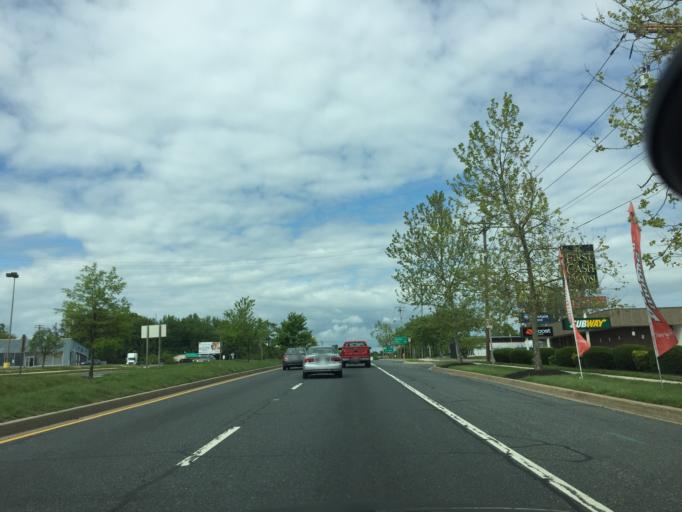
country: US
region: Maryland
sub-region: Baltimore County
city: Essex
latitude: 39.3152
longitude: -76.4612
